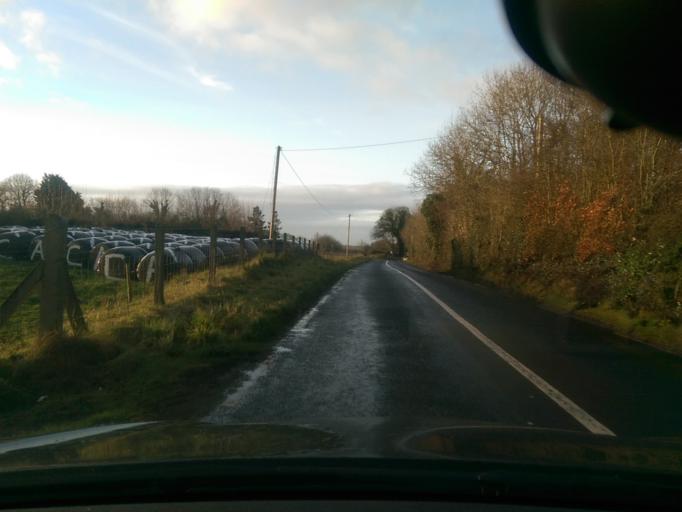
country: IE
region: Connaught
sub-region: County Galway
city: Athenry
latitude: 53.3992
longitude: -8.6522
